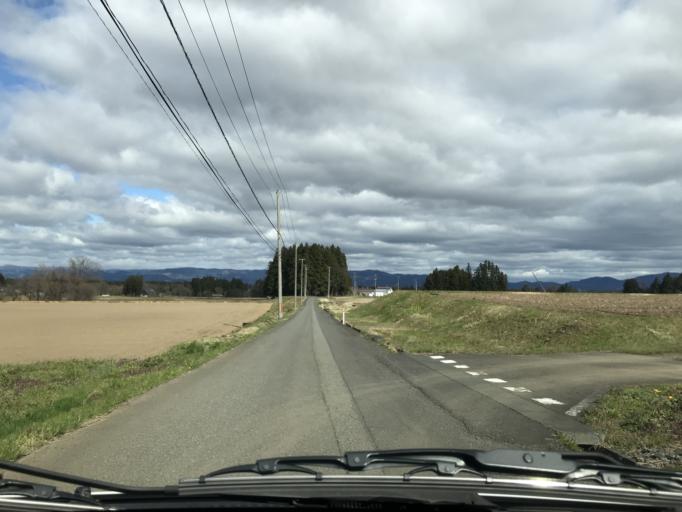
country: JP
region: Iwate
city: Mizusawa
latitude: 39.1057
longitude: 141.0292
